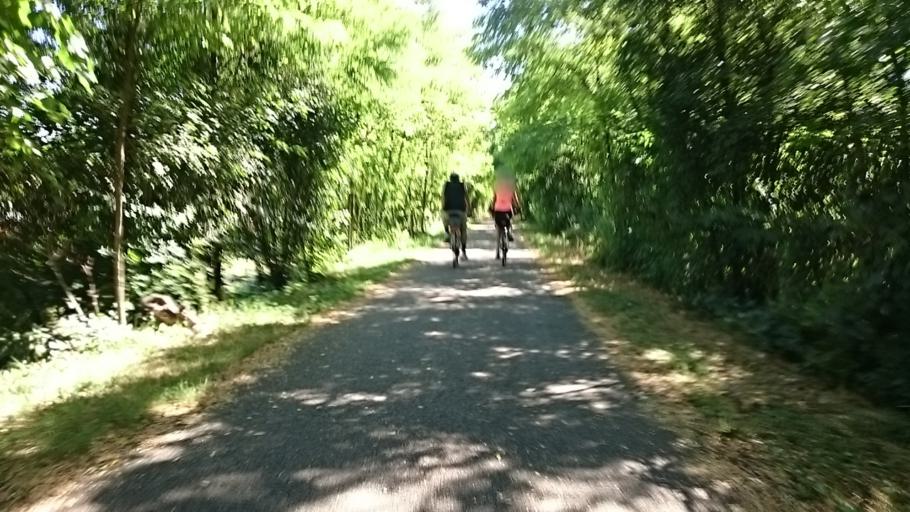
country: IT
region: Veneto
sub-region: Provincia di Padova
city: Piombino Dese
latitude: 45.6007
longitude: 12.0006
